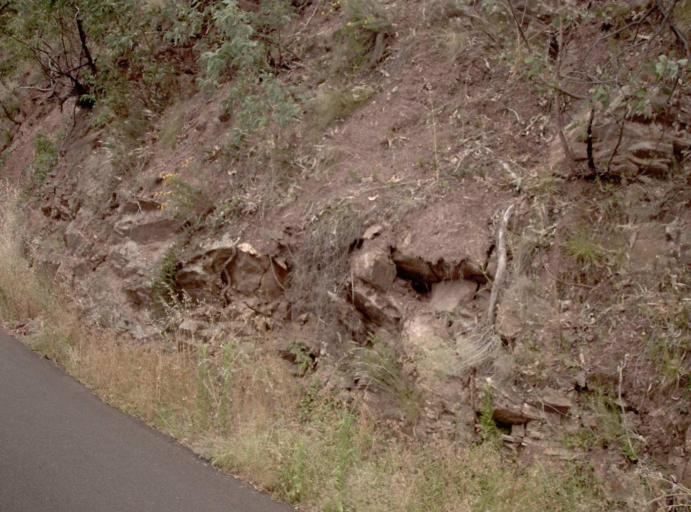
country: AU
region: Victoria
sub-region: Wellington
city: Heyfield
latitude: -37.7066
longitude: 146.6668
